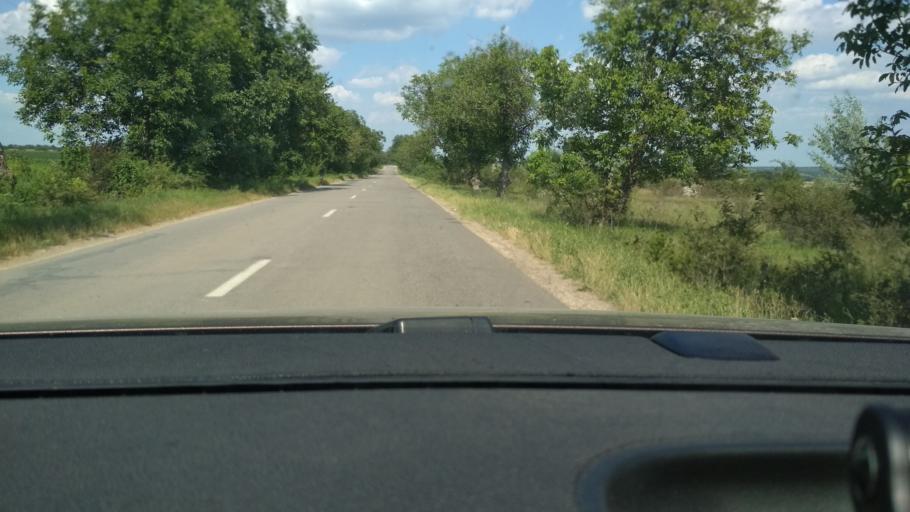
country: MD
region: Criuleni
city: Criuleni
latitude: 47.1660
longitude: 29.1773
